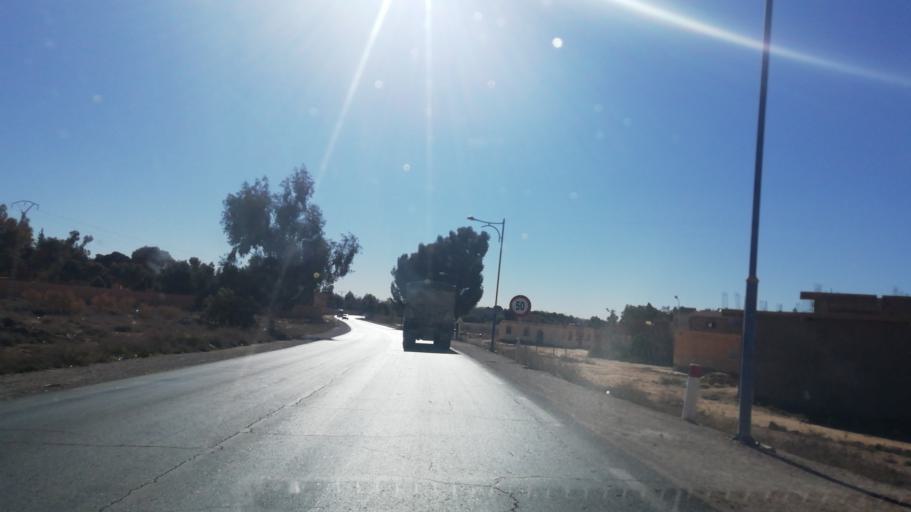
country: DZ
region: Saida
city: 'Ain el Hadjar
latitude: 34.1474
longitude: 0.0701
